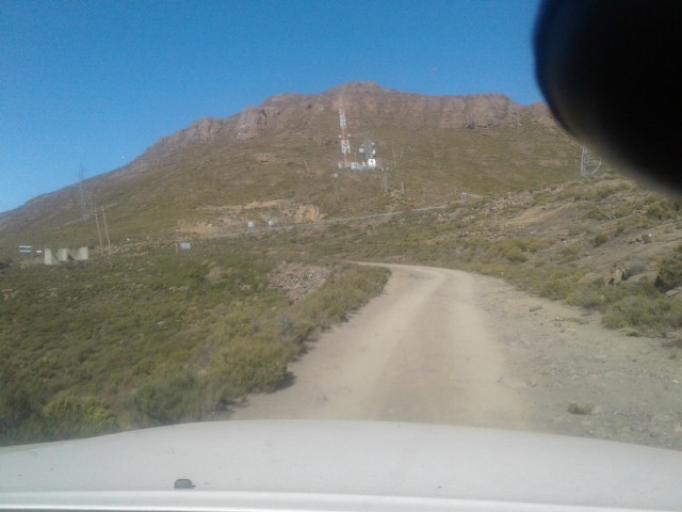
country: LS
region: Maseru
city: Nako
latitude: -29.4300
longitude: 27.9679
